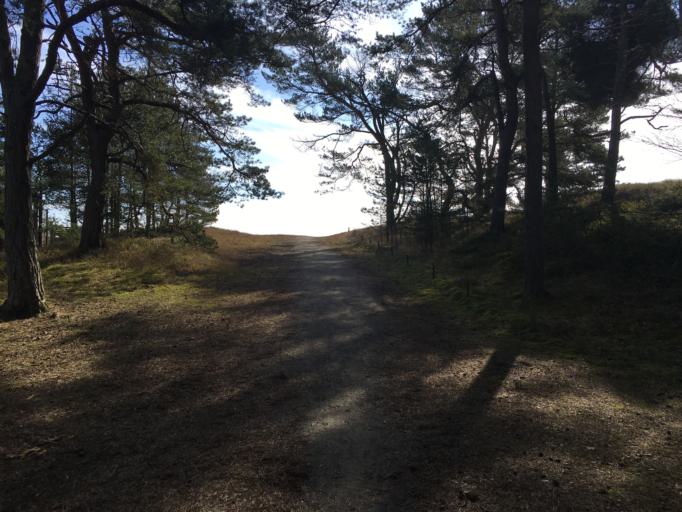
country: SE
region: Skane
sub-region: Kristianstads Kommun
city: Ahus
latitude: 55.8745
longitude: 14.2477
